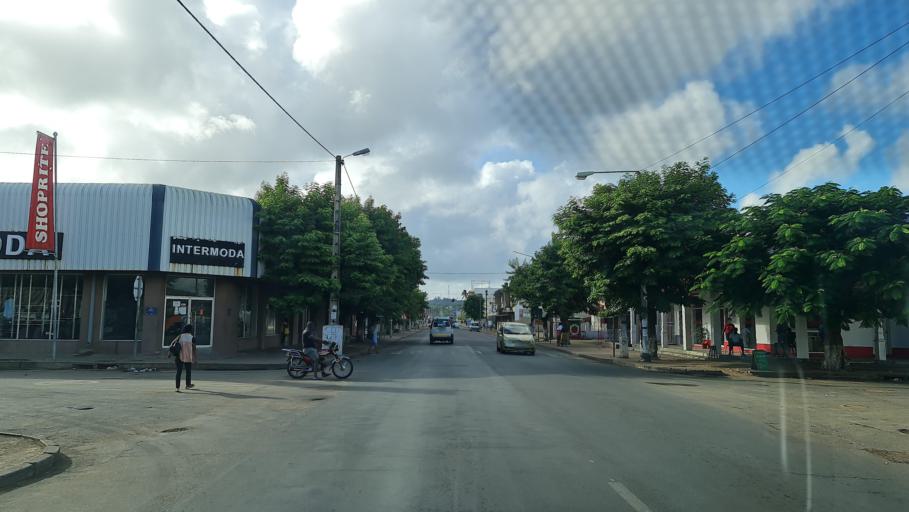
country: MZ
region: Gaza
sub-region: Xai-Xai District
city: Xai-Xai
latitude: -25.0449
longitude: 33.6432
